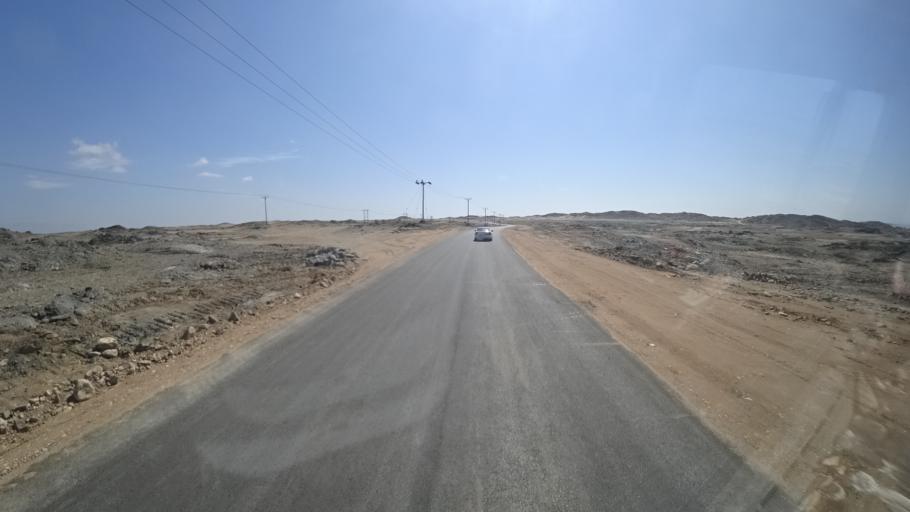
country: OM
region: Zufar
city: Salalah
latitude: 16.9659
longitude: 54.7543
